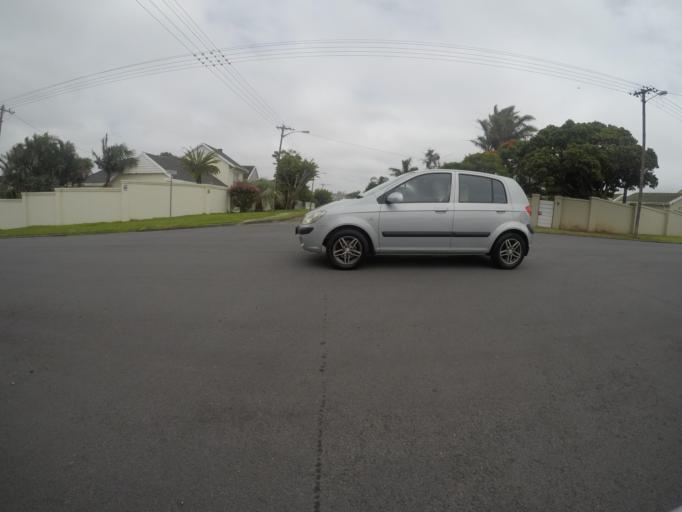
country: ZA
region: Eastern Cape
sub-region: Buffalo City Metropolitan Municipality
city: East London
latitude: -32.9897
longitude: 27.9332
